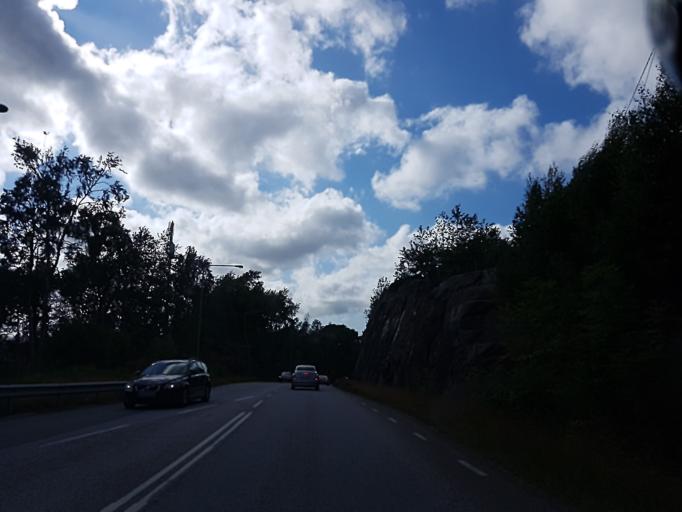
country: SE
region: Vaestra Goetaland
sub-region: Goteborg
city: Eriksbo
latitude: 57.7250
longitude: 12.0423
